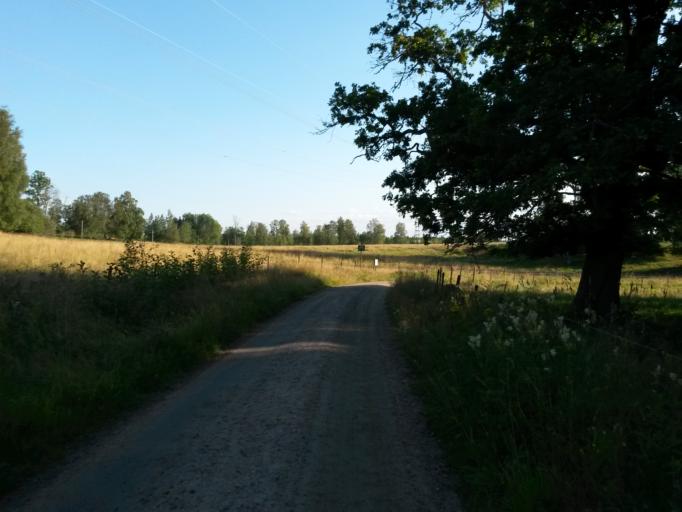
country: SE
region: Vaestra Goetaland
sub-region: Vargarda Kommun
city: Vargarda
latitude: 58.0174
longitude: 12.8218
